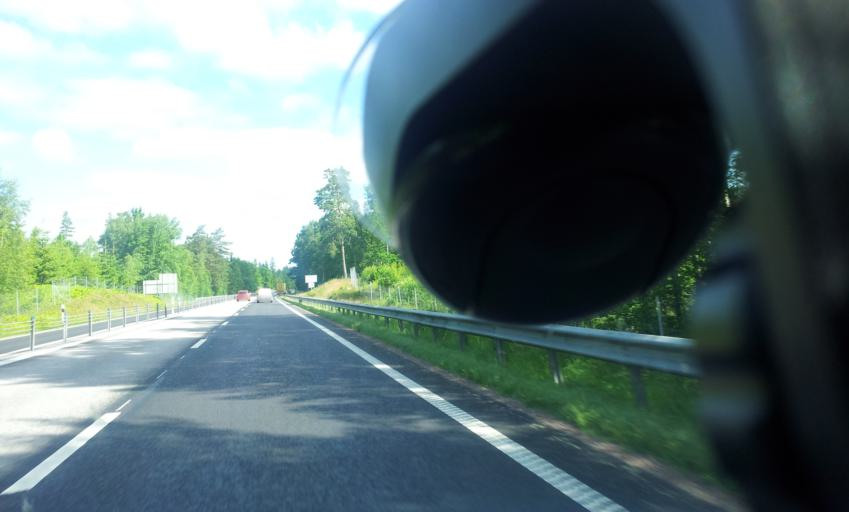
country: SE
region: Kalmar
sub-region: Monsteras Kommun
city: Timmernabben
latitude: 56.8972
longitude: 16.3797
